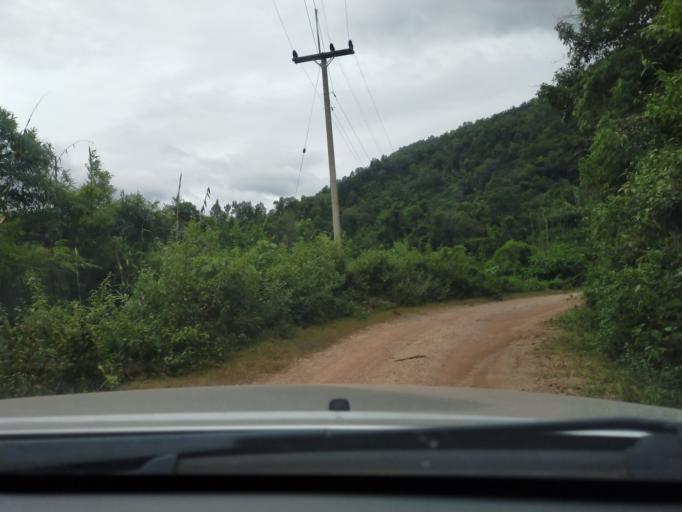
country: TH
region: Nan
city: Chaloem Phra Kiat
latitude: 19.7983
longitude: 101.3627
